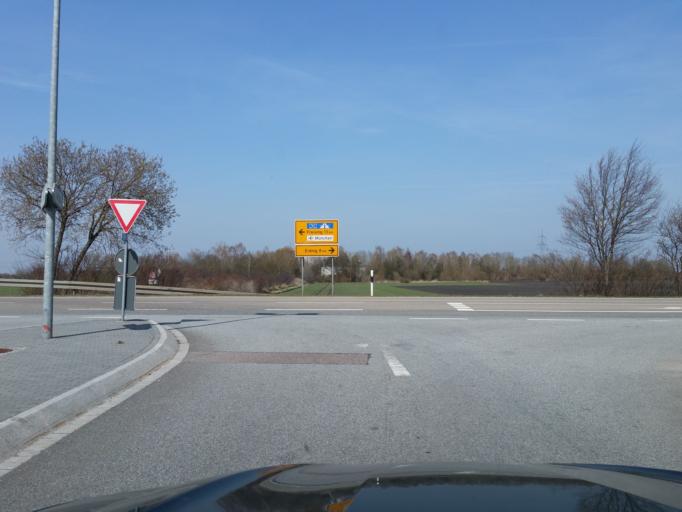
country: DE
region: Bavaria
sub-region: Upper Bavaria
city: Eitting
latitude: 48.3716
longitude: 11.8916
